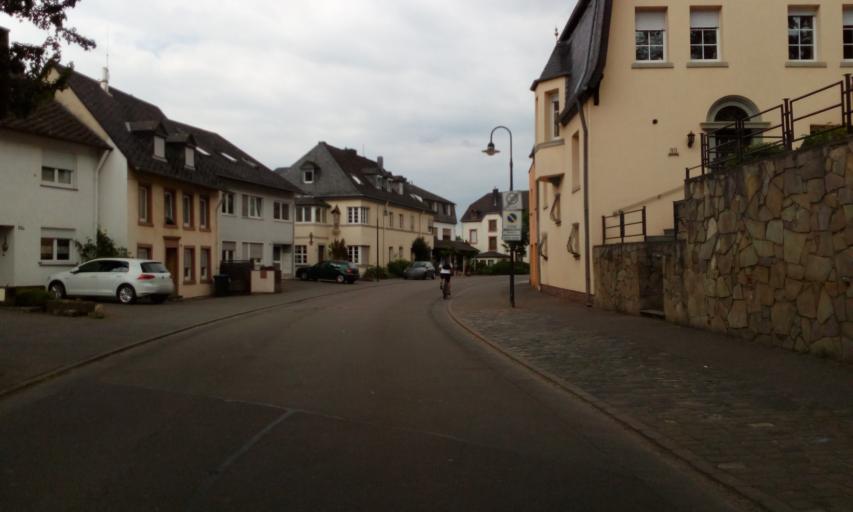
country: DE
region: Rheinland-Pfalz
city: Kenn
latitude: 49.7863
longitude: 6.7079
